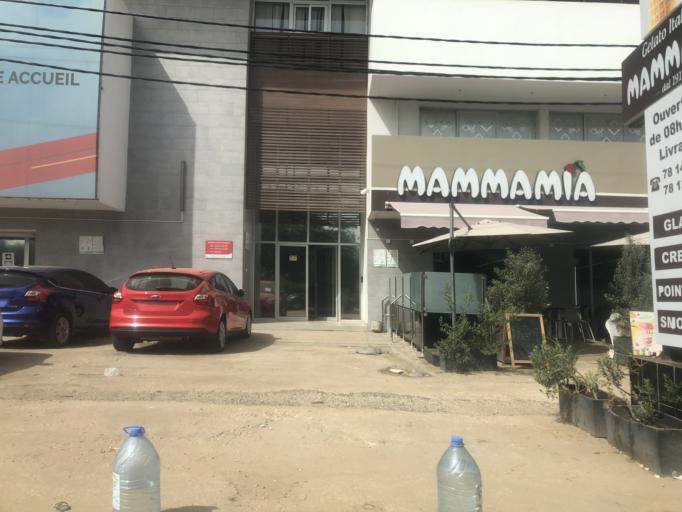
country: SN
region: Dakar
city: Mermoz Boabab
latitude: 14.7371
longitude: -17.5099
